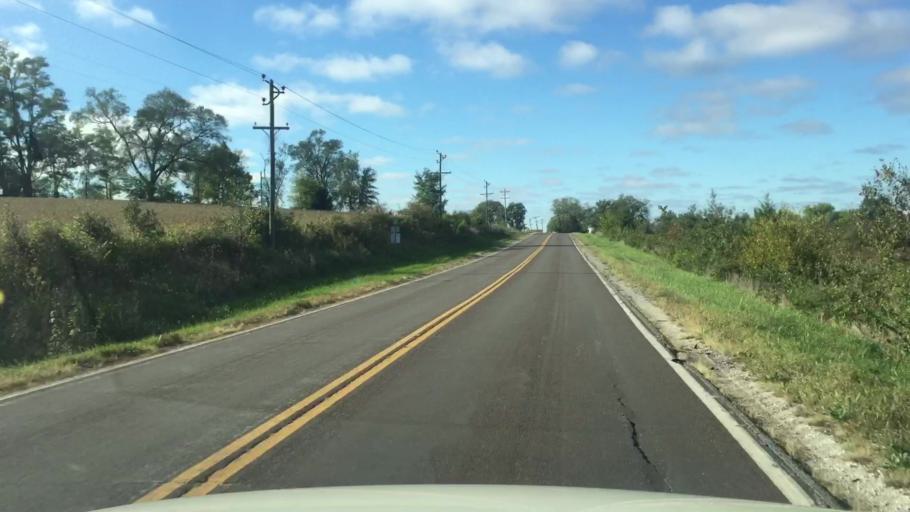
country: US
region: Missouri
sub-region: Howard County
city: Fayette
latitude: 39.1022
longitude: -92.7352
